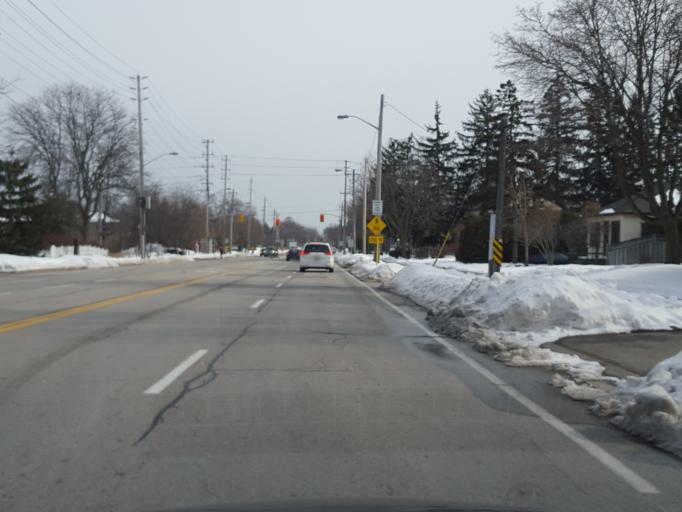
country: CA
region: Ontario
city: Burlington
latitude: 43.3558
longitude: -79.7737
